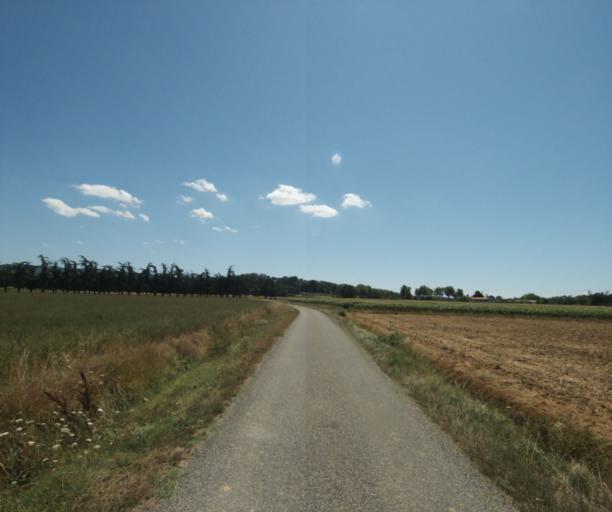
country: FR
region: Midi-Pyrenees
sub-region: Departement de la Haute-Garonne
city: Revel
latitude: 43.4497
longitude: 1.9493
